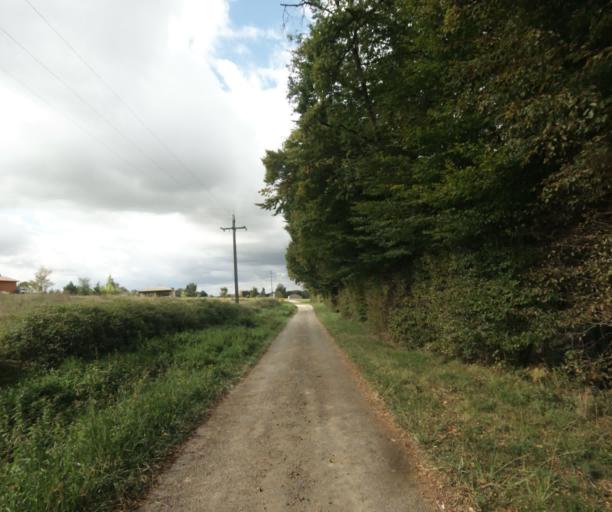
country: FR
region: Midi-Pyrenees
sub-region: Departement du Gers
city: Eauze
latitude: 43.8522
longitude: 0.0518
